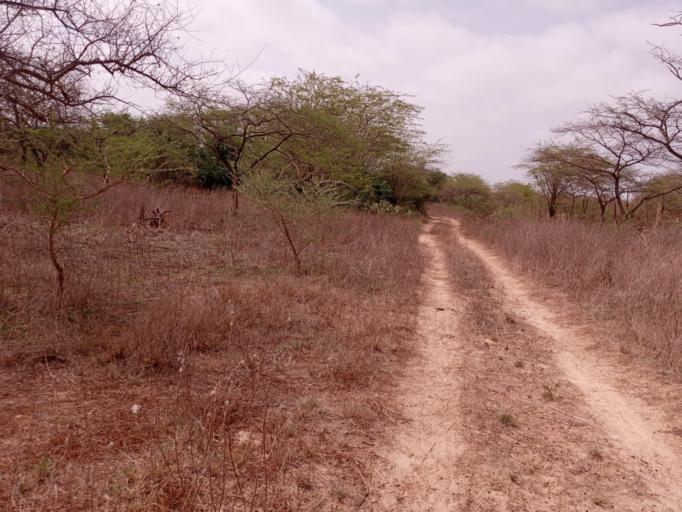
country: SN
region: Saint-Louis
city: Saint-Louis
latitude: 15.9189
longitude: -16.4531
